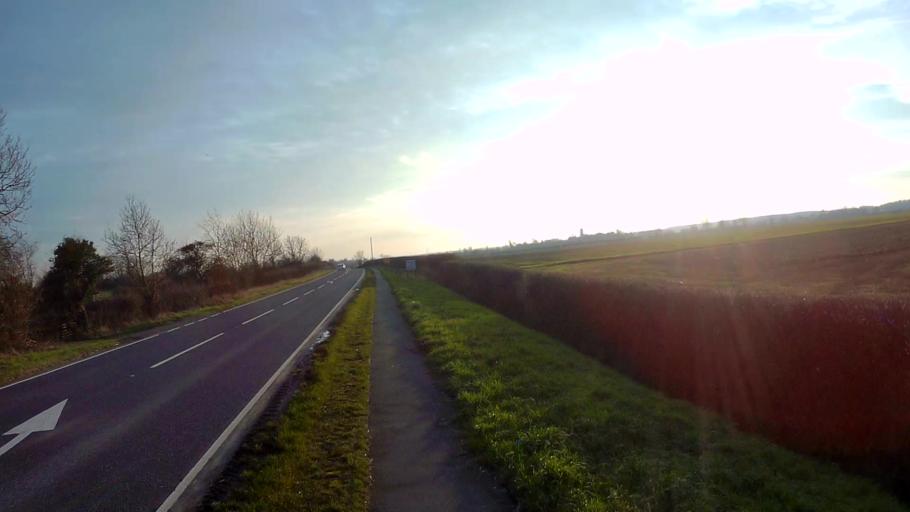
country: GB
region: England
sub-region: Lincolnshire
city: Bourne
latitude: 52.7919
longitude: -0.3762
